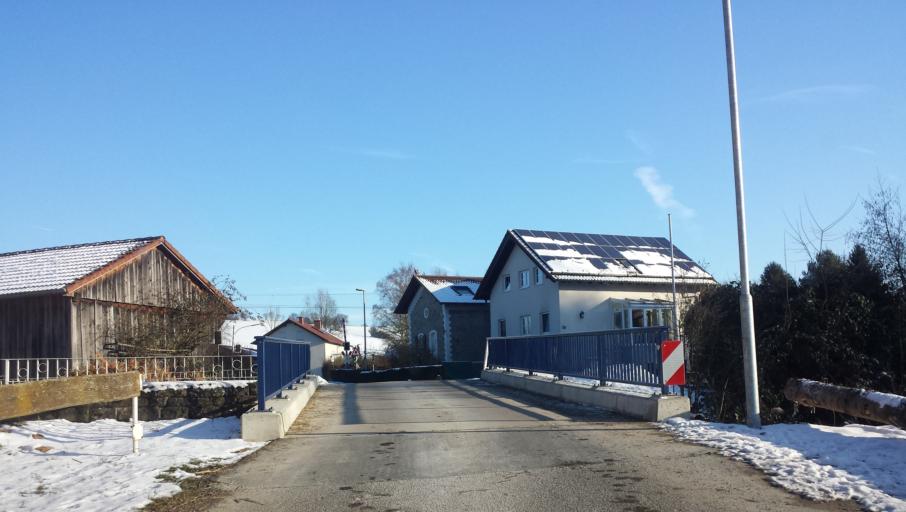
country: DE
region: Baden-Wuerttemberg
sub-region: Karlsruhe Region
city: Neidenstein
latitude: 49.3145
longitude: 8.8908
